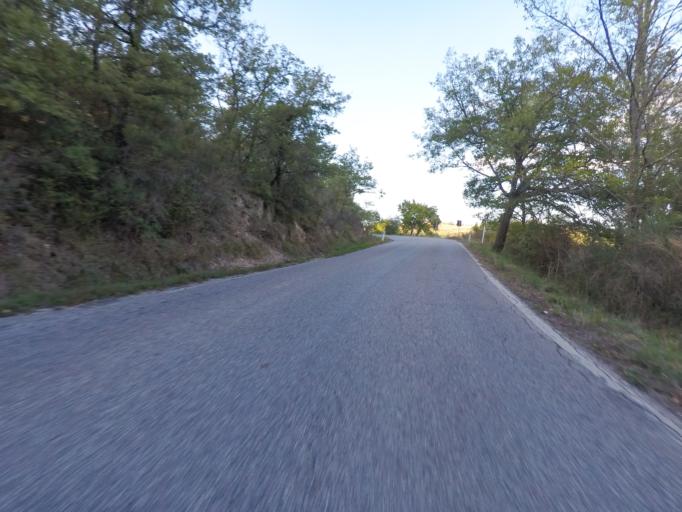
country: IT
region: Tuscany
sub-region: Provincia di Siena
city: Radda in Chianti
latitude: 43.4782
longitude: 11.3698
